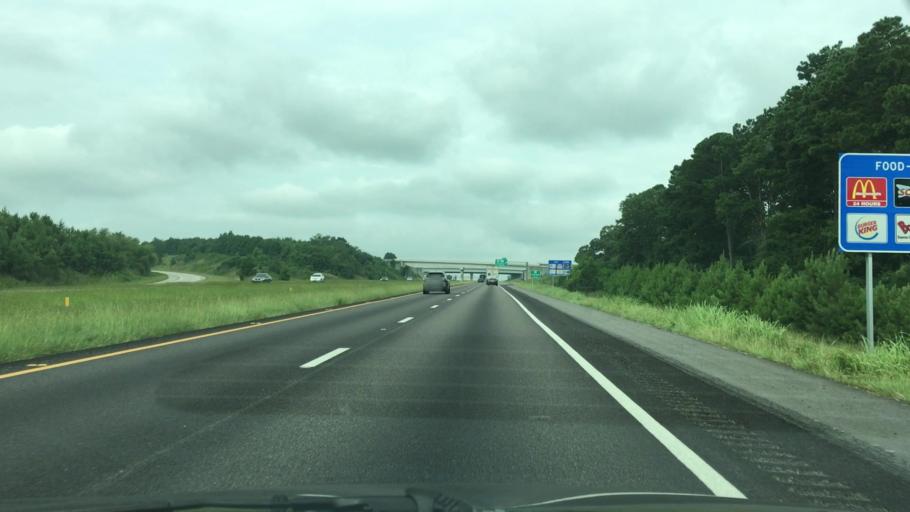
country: US
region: South Carolina
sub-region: Edgefield County
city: Murphys Estates
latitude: 33.5690
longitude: -81.9215
